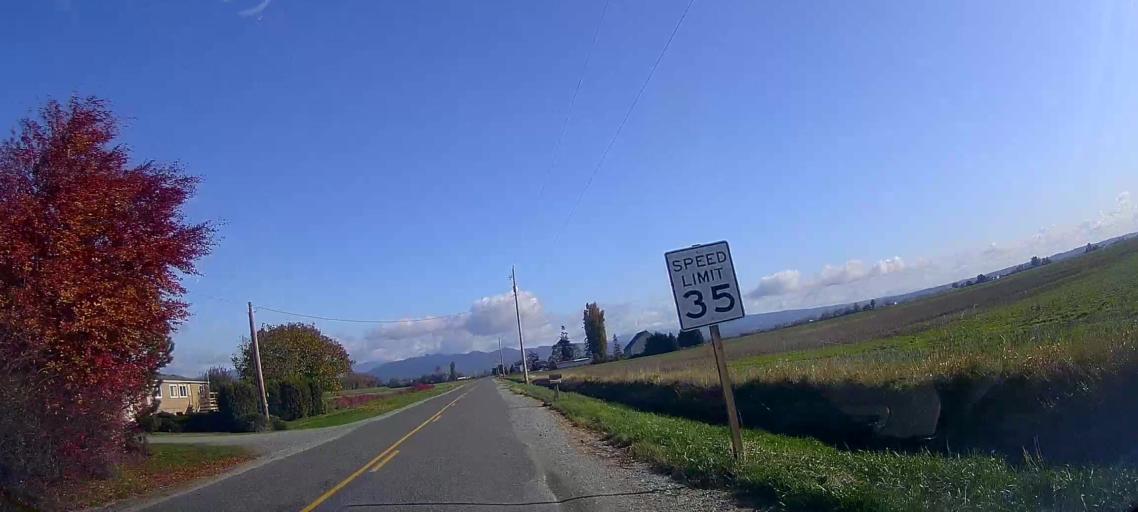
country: US
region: Washington
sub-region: Skagit County
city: Mount Vernon
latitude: 48.3556
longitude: -122.4376
